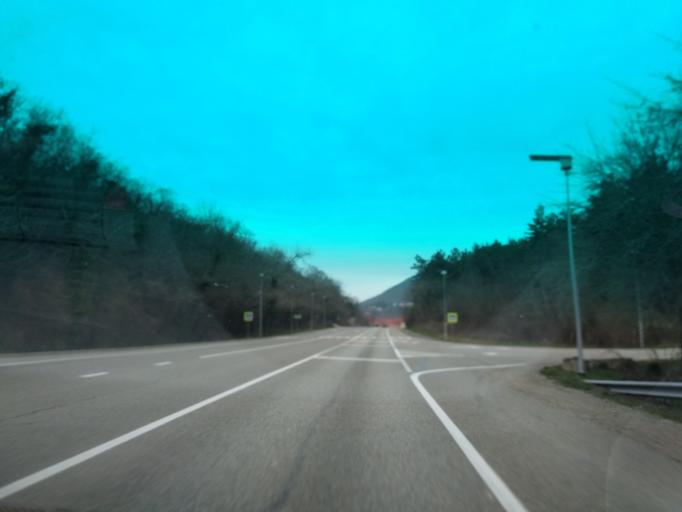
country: RU
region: Krasnodarskiy
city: Ol'ginka
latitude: 44.1882
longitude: 38.8914
